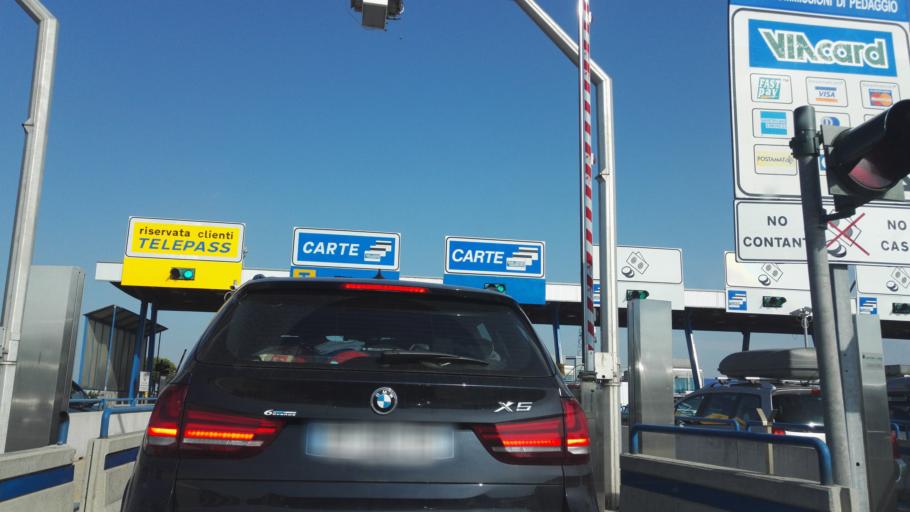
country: IT
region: Apulia
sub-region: Provincia di Bari
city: Modugno
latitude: 41.0925
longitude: 16.7773
